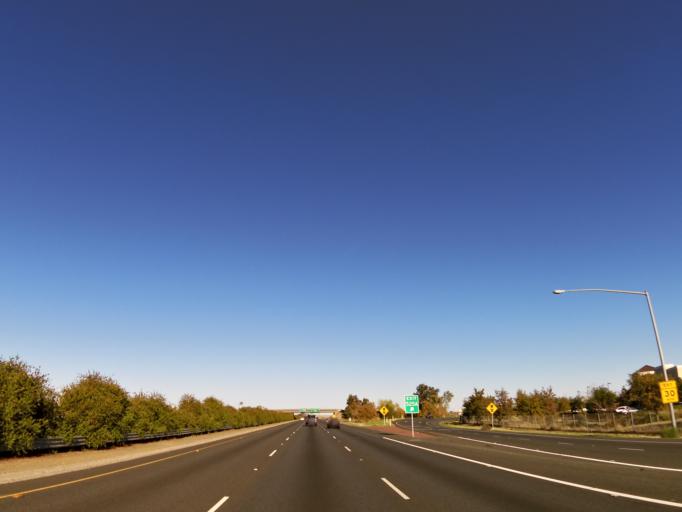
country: US
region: California
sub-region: Yolo County
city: West Sacramento
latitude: 38.6524
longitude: -121.5311
